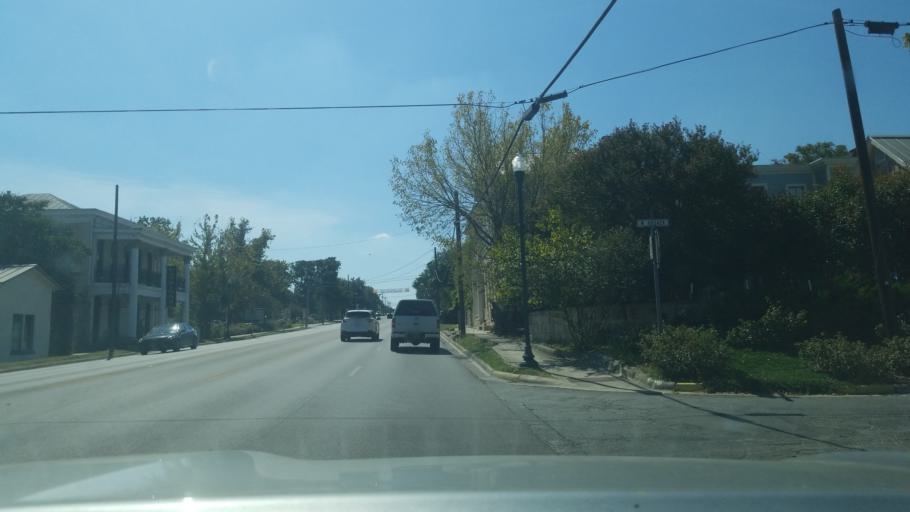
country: US
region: Texas
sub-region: Kendall County
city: Boerne
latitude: 29.7874
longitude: -98.7291
